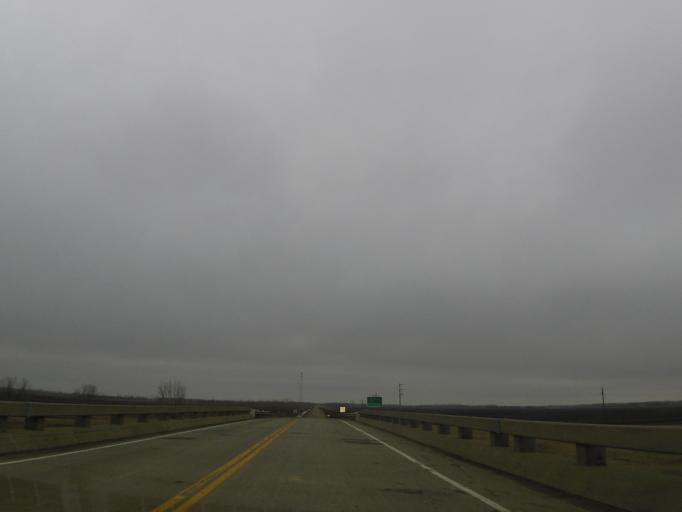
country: US
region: North Dakota
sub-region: Walsh County
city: Grafton
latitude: 48.3532
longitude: -97.1898
